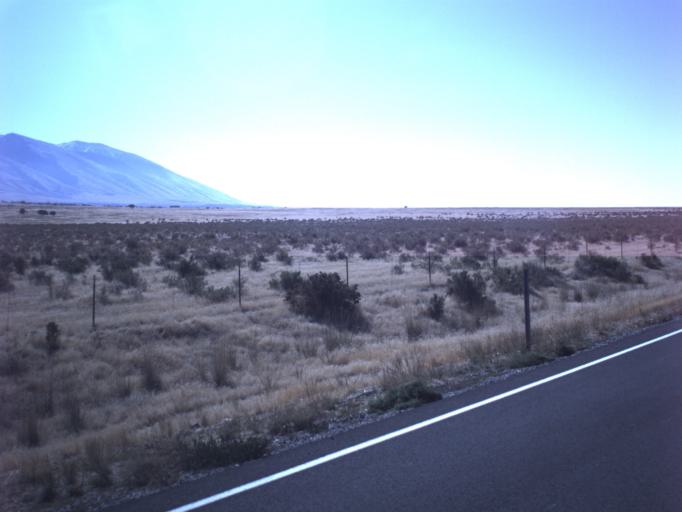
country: US
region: Utah
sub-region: Tooele County
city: Grantsville
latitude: 40.5493
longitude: -112.7411
